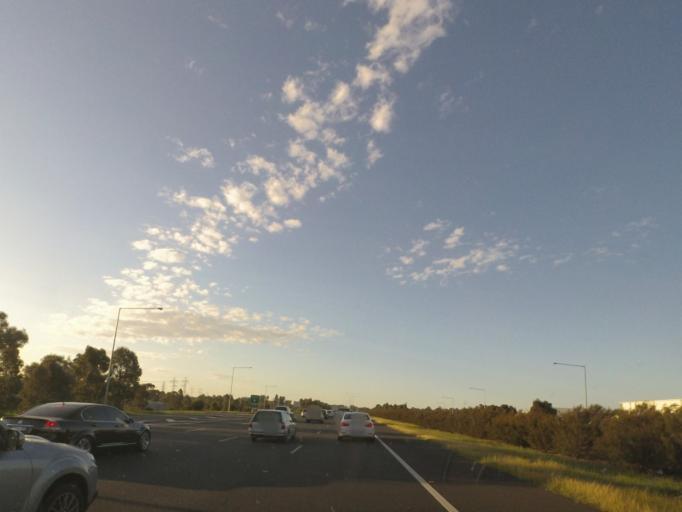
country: AU
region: Victoria
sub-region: Monash
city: Mulgrave
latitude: -37.9070
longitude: 145.2158
